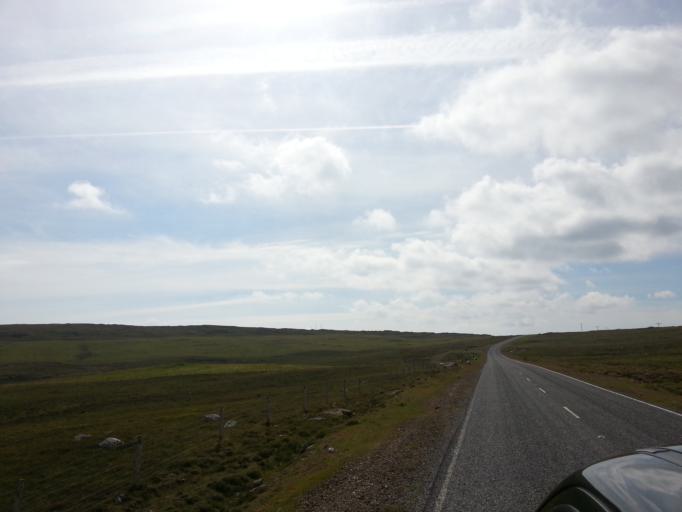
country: GB
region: Scotland
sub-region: Shetland Islands
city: Shetland
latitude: 60.6941
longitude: -0.9354
